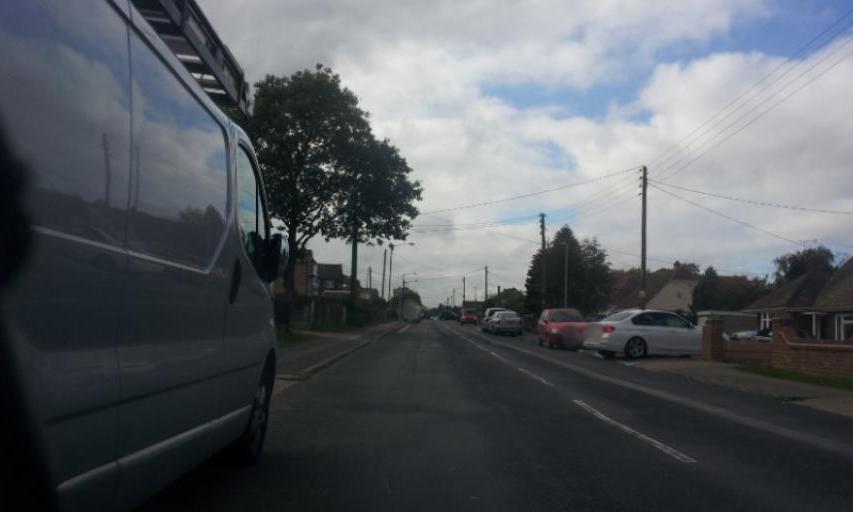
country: GB
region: England
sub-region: Kent
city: Chatham
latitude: 51.3431
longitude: 0.5191
